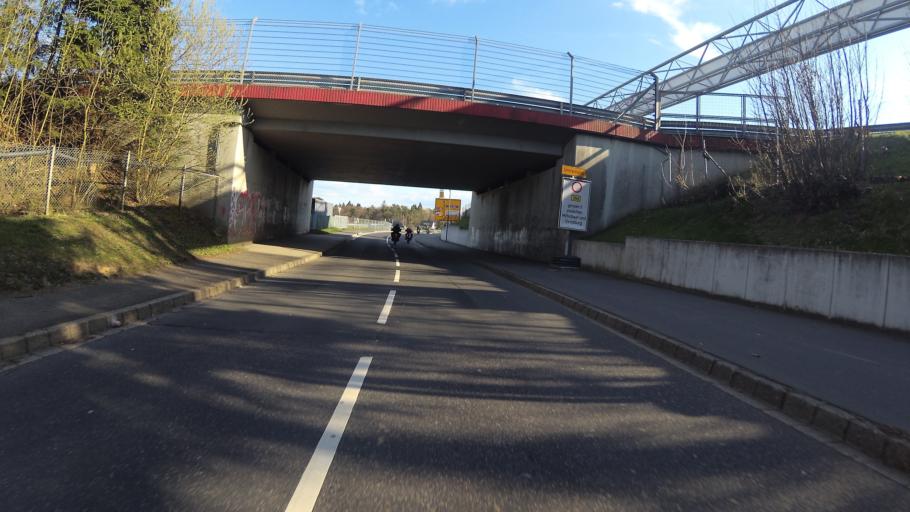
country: DE
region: Rheinland-Pfalz
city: Nurburg
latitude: 50.3380
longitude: 6.9512
